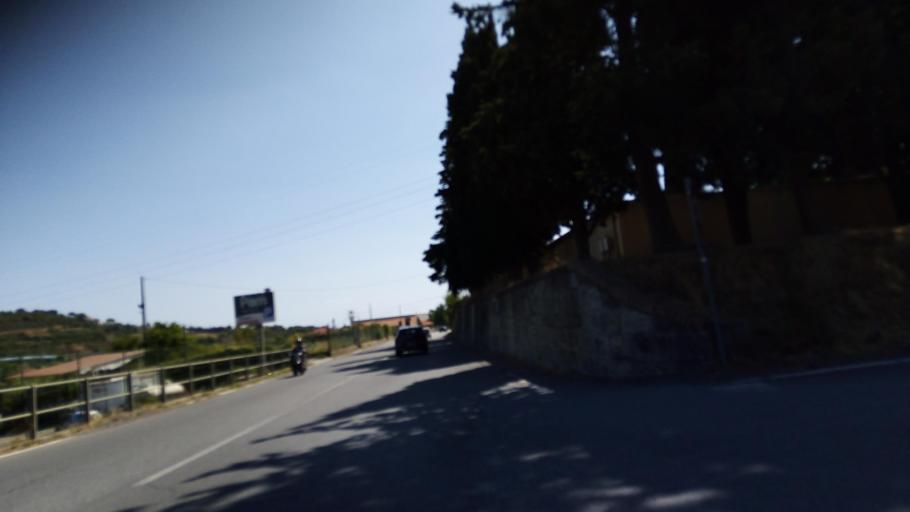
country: IT
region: Liguria
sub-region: Provincia di Savona
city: Toirano
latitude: 44.1215
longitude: 8.2161
